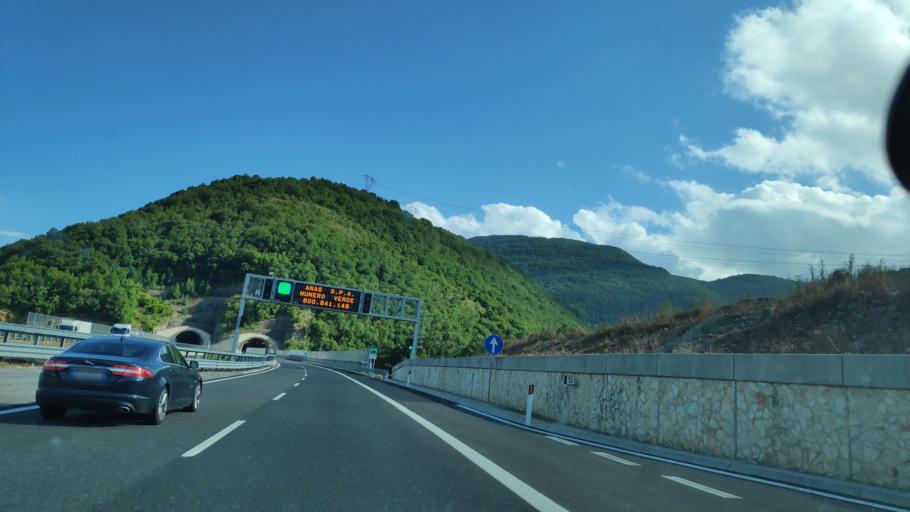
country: IT
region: Campania
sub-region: Provincia di Salerno
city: Casalbuono
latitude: 40.2164
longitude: 15.6719
